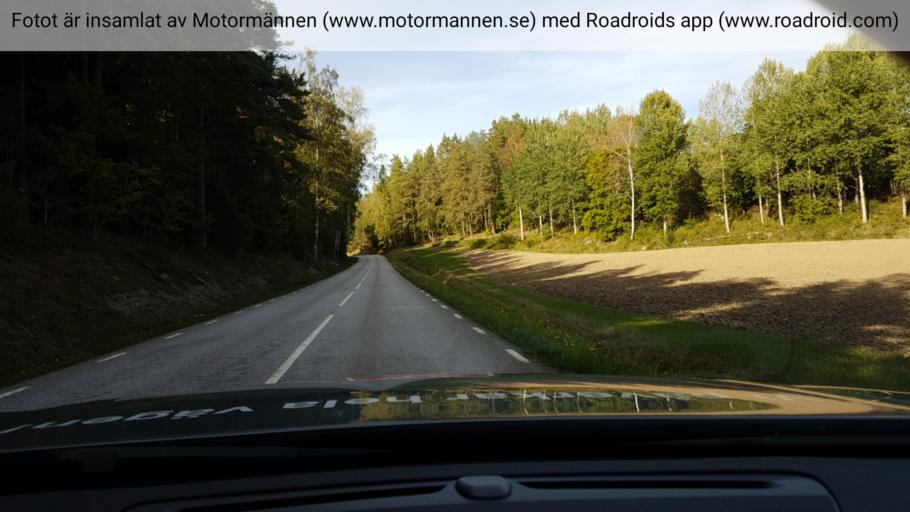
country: SE
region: OEstergoetland
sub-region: Valdemarsviks Kommun
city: Valdemarsvik
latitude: 58.1620
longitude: 16.6039
